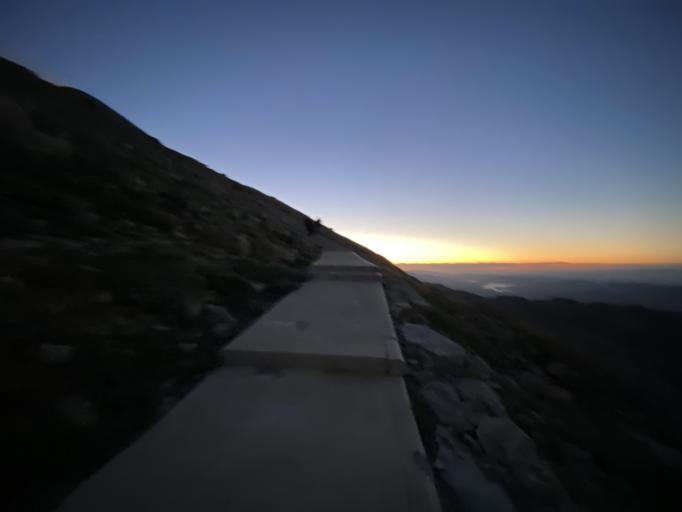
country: TR
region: Adiyaman
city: Narince
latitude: 37.9787
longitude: 38.7403
